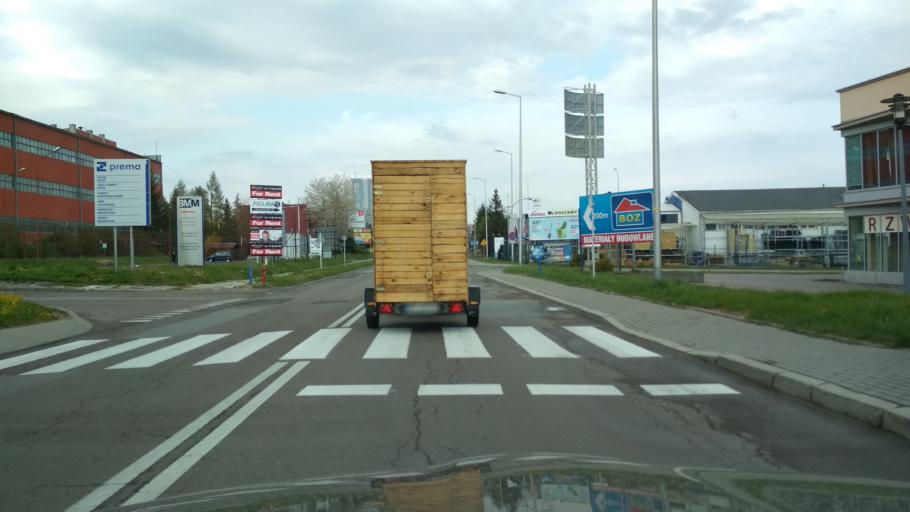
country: PL
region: Subcarpathian Voivodeship
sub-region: Rzeszow
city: Rzeszow
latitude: 50.0235
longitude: 21.9713
